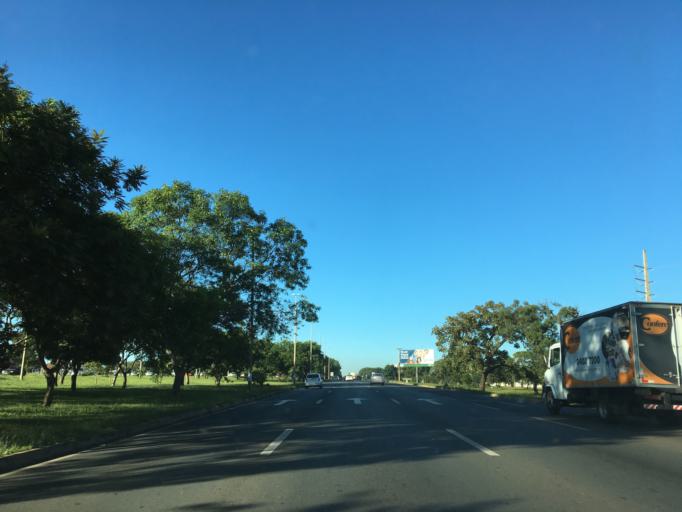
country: BR
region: Federal District
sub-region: Brasilia
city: Brasilia
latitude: -15.7633
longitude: -47.9317
